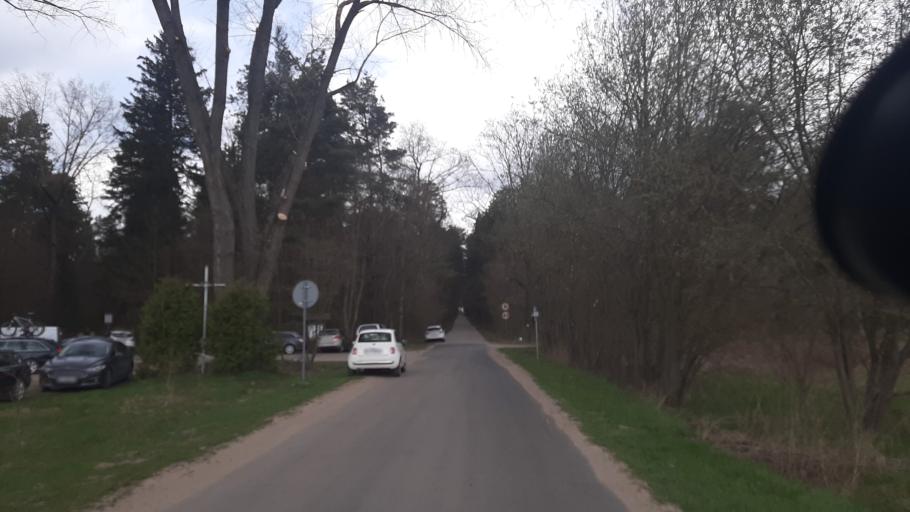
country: PL
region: Lublin Voivodeship
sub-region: Powiat lubelski
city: Niemce
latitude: 51.3682
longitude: 22.5524
